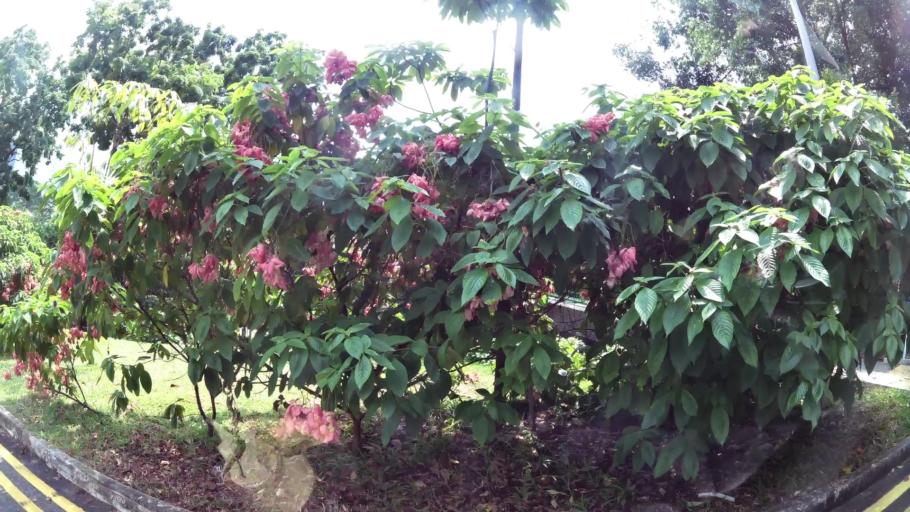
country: SG
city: Singapore
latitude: 1.2816
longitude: 103.8311
